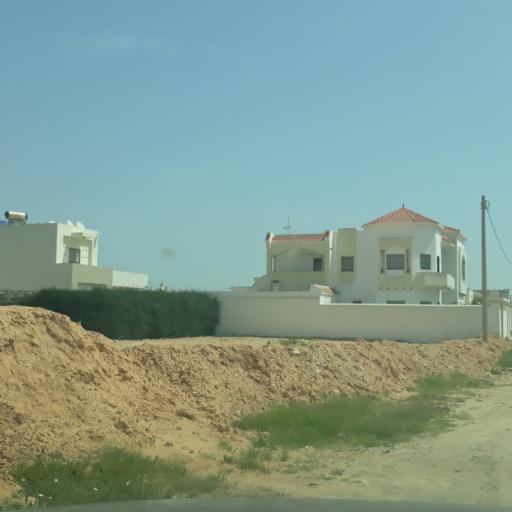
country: TN
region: Safaqis
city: Al Qarmadah
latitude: 34.7937
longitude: 10.7606
